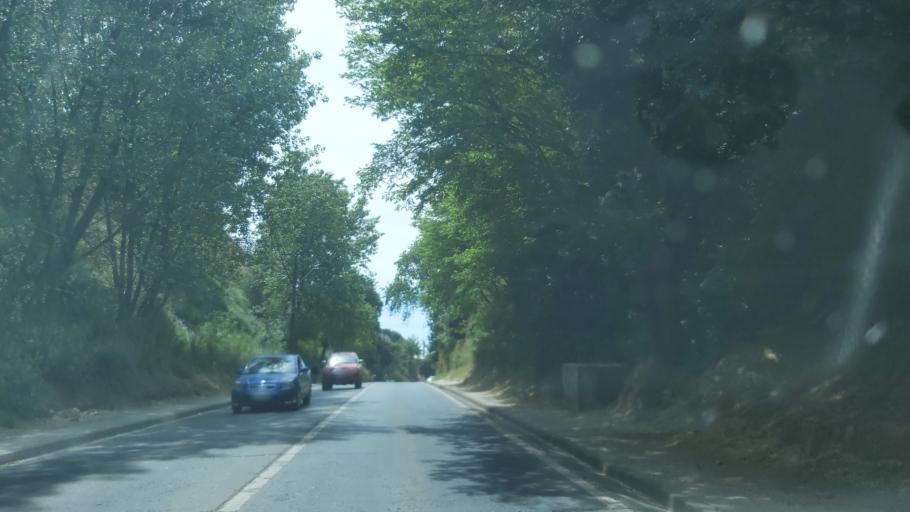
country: CL
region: Maule
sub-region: Provincia de Talca
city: Constitucion
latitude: -35.3295
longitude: -72.4191
